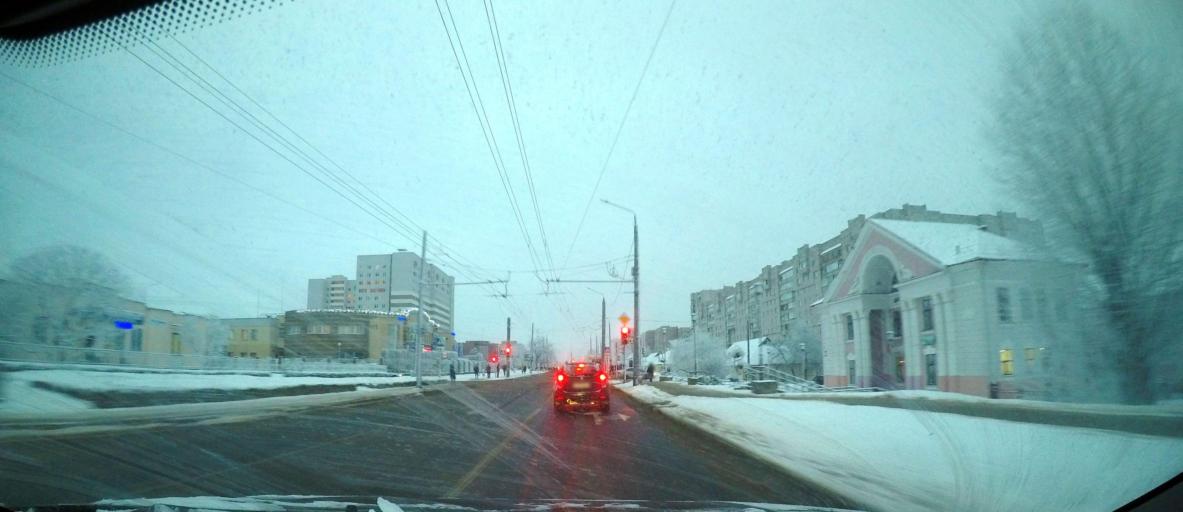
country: BY
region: Grodnenskaya
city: Hrodna
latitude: 53.6984
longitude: 23.8399
